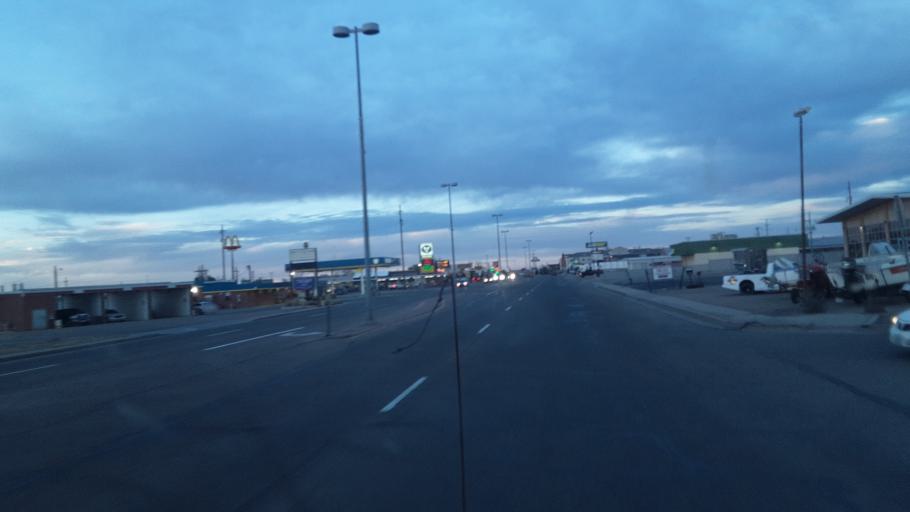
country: US
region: Colorado
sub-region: Prowers County
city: Lamar
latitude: 38.0973
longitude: -102.6194
